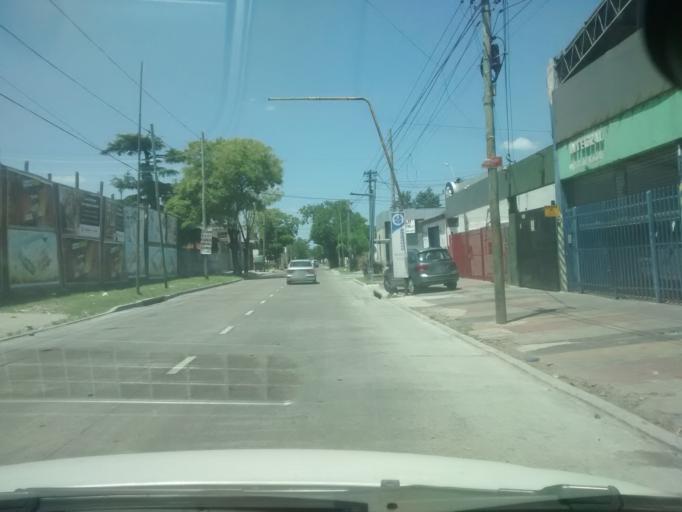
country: AR
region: Buenos Aires
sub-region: Partido de Moron
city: Moron
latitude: -34.6608
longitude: -58.6070
